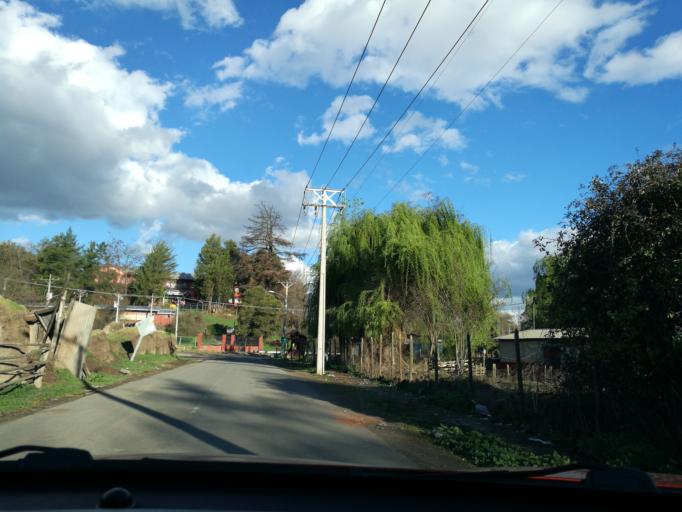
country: CL
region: O'Higgins
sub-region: Provincia de Cachapoal
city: Graneros
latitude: -34.1010
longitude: -70.8101
